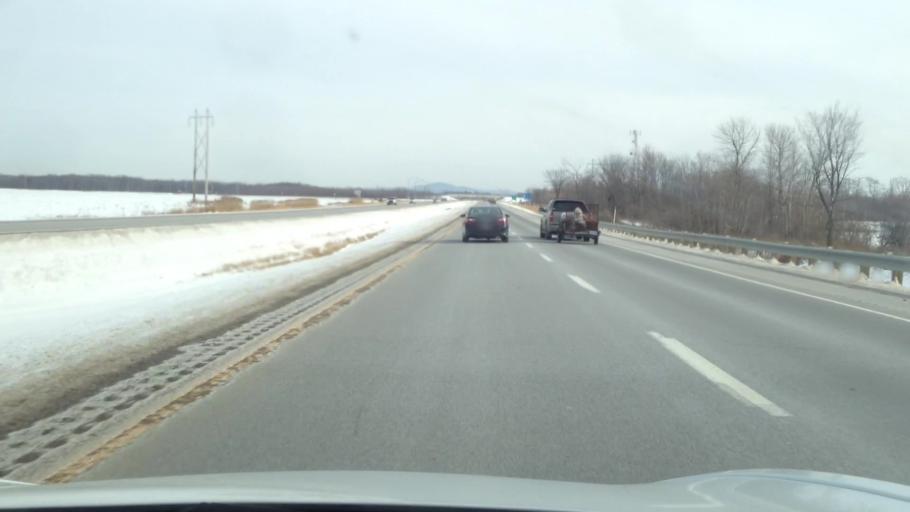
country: CA
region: Quebec
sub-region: Monteregie
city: Rigaud
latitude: 45.4865
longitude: -74.3282
